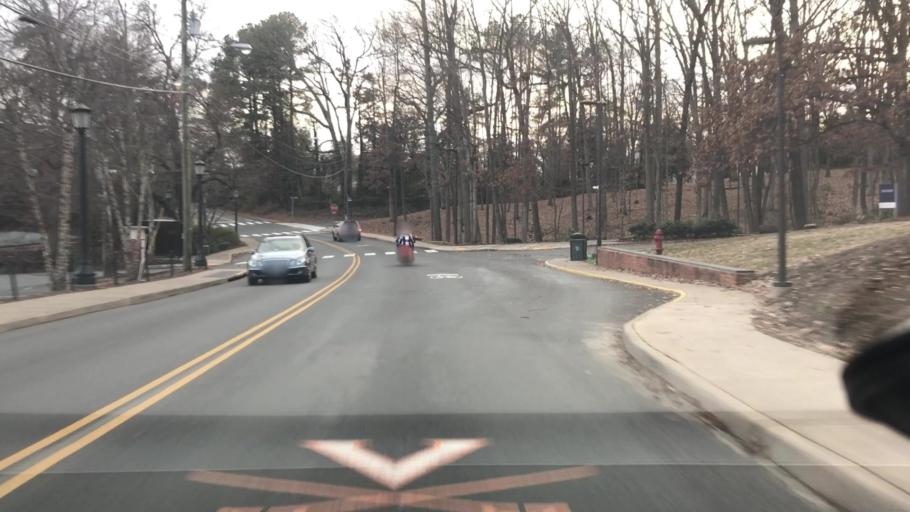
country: US
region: Virginia
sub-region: City of Charlottesville
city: Charlottesville
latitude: 38.0296
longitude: -78.5163
